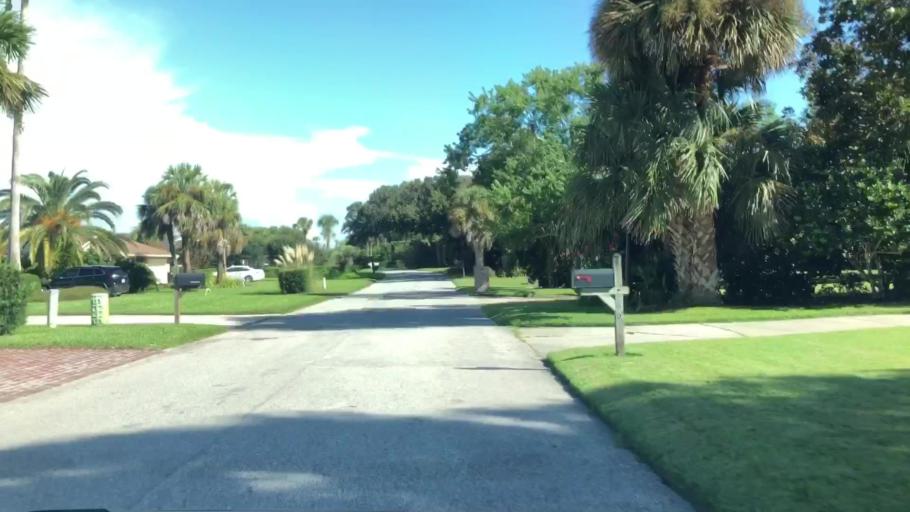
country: US
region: Florida
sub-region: Saint Johns County
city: Ponte Vedra Beach
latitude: 30.2342
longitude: -81.3799
